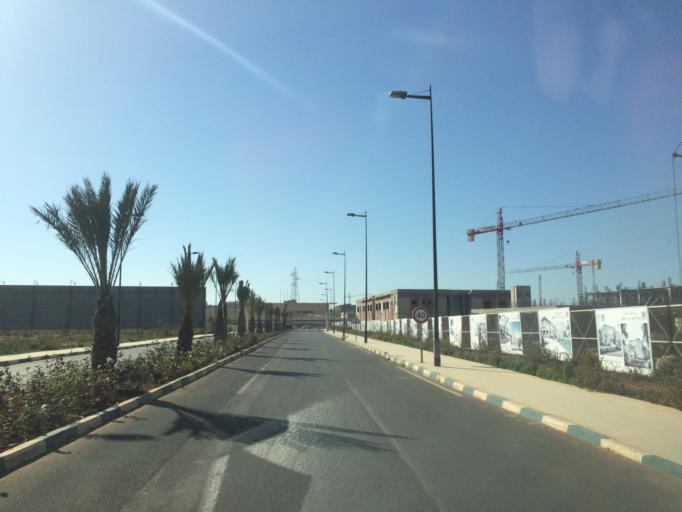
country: MA
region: Rabat-Sale-Zemmour-Zaer
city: Sale
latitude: 33.9861
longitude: -6.7254
